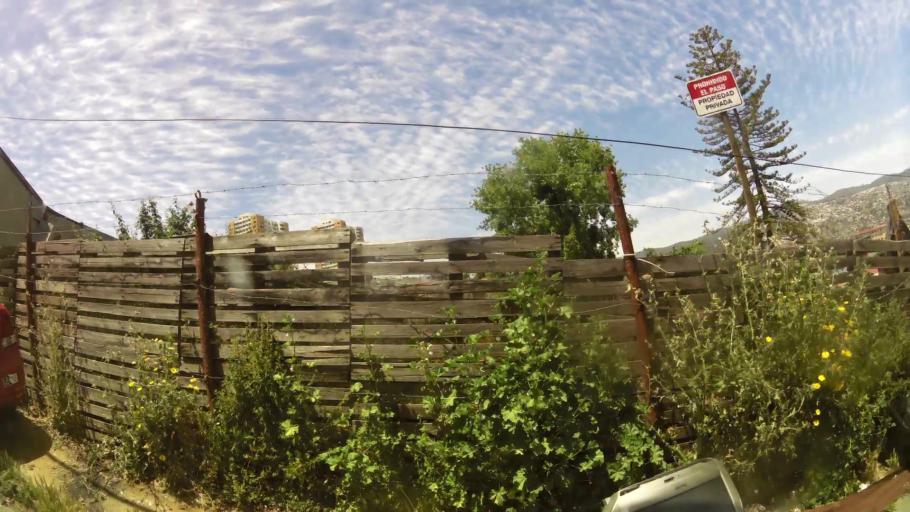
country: CL
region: Valparaiso
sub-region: Provincia de Valparaiso
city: Valparaiso
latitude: -33.0441
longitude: -71.5993
